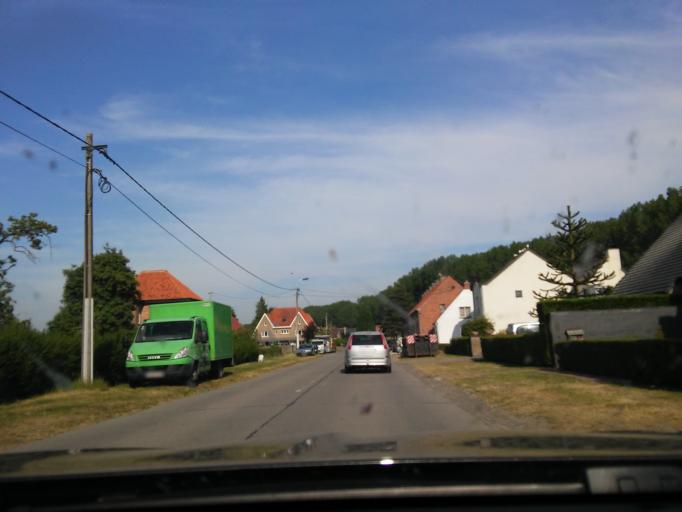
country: BE
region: Flanders
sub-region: Provincie Oost-Vlaanderen
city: Sint-Laureins
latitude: 51.2447
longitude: 3.5118
